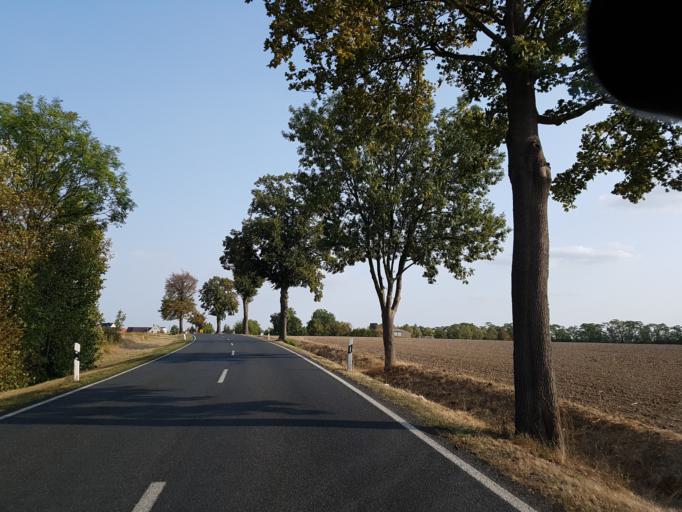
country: DE
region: Saxony
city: Elsnig
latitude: 51.5997
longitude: 12.9422
